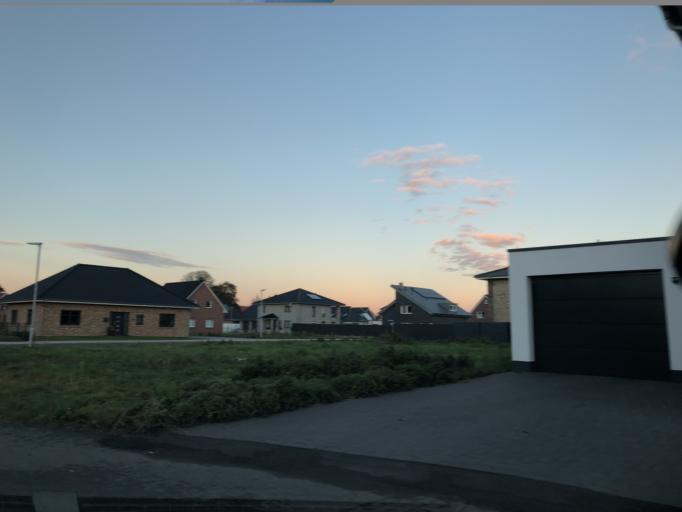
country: DE
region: Lower Saxony
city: Papenburg
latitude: 53.0804
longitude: 7.4123
